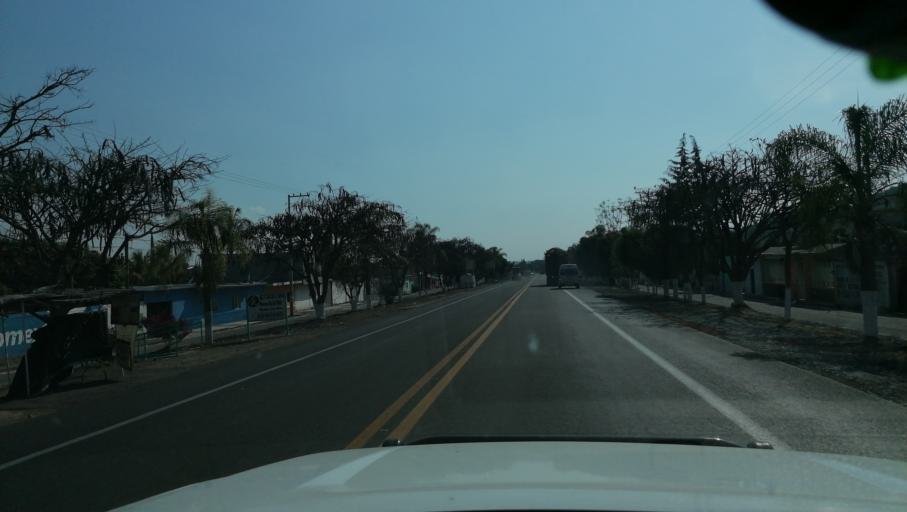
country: MX
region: Puebla
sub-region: Izucar de Matamoros
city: La Galarza
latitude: 18.6744
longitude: -98.4462
